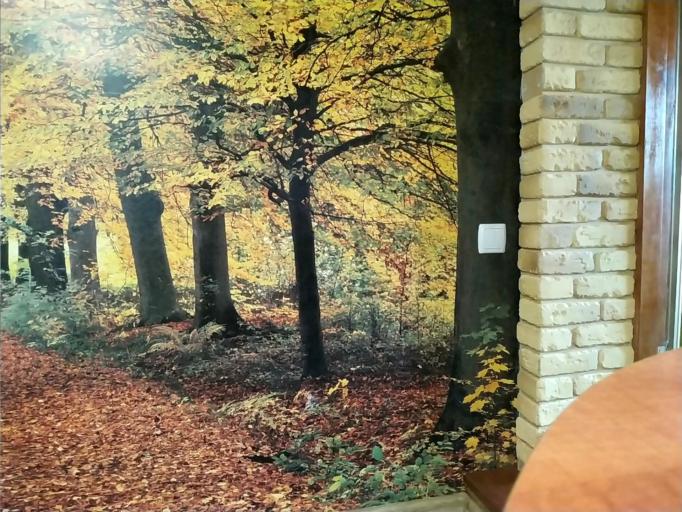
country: RU
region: Leningrad
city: Tolmachevo
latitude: 58.9339
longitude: 29.7030
